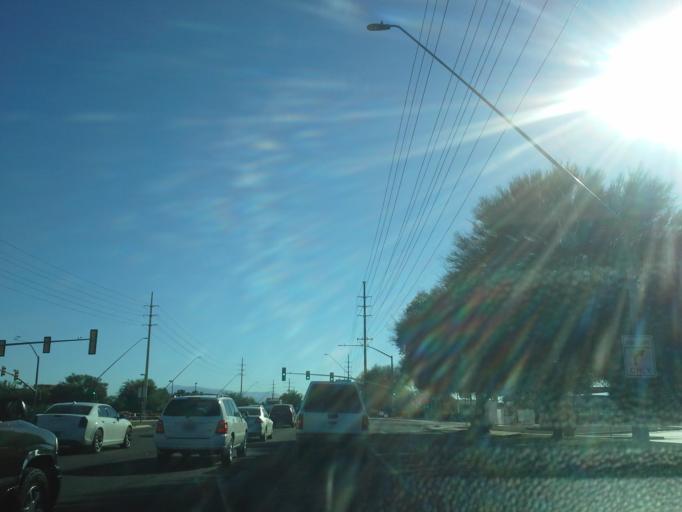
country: US
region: Arizona
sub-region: Pima County
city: Drexel Heights
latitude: 32.1337
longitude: -110.9998
